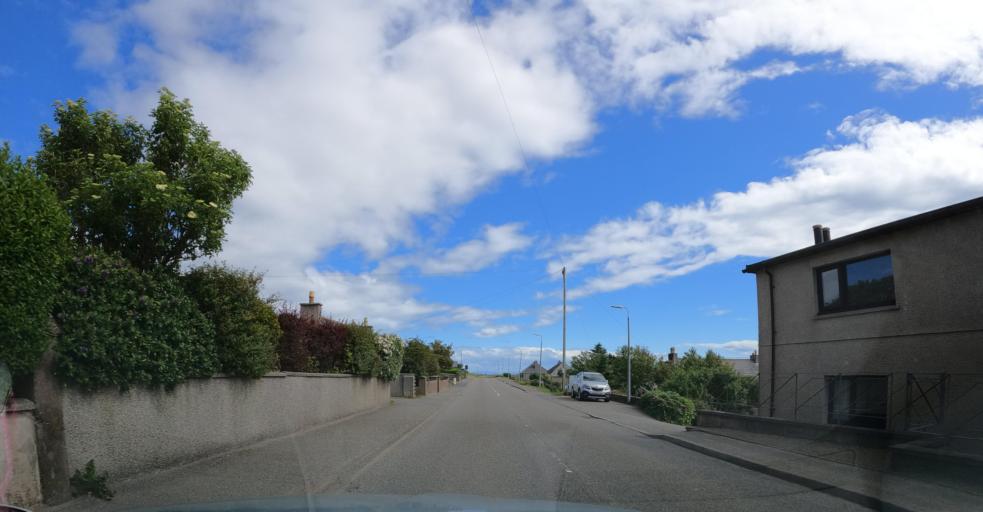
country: GB
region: Scotland
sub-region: Eilean Siar
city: Stornoway
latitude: 58.2046
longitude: -6.3525
